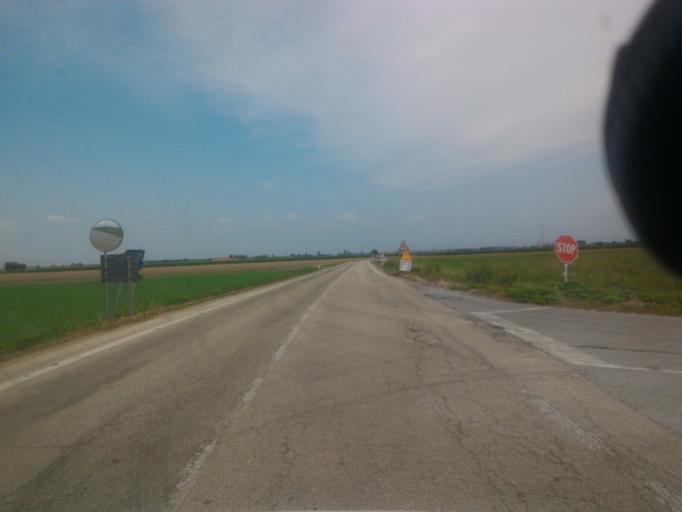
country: IT
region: Piedmont
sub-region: Provincia di Torino
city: Buriasco
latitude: 44.8543
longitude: 7.4502
